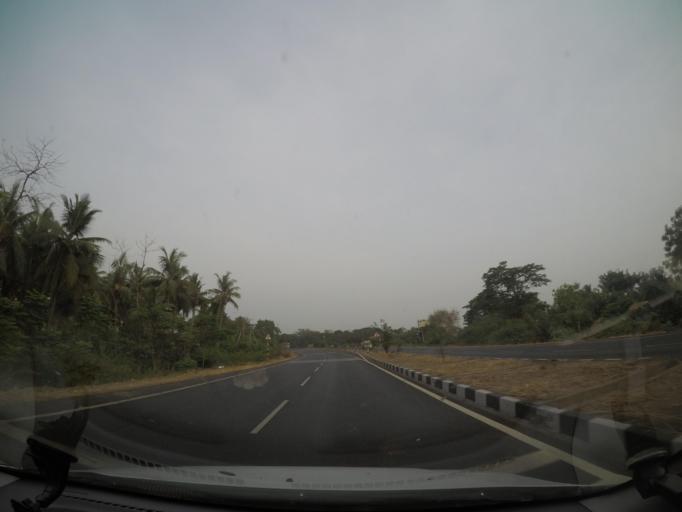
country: IN
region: Andhra Pradesh
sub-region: Krishna
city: Gannavaram
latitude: 16.6107
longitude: 80.9143
